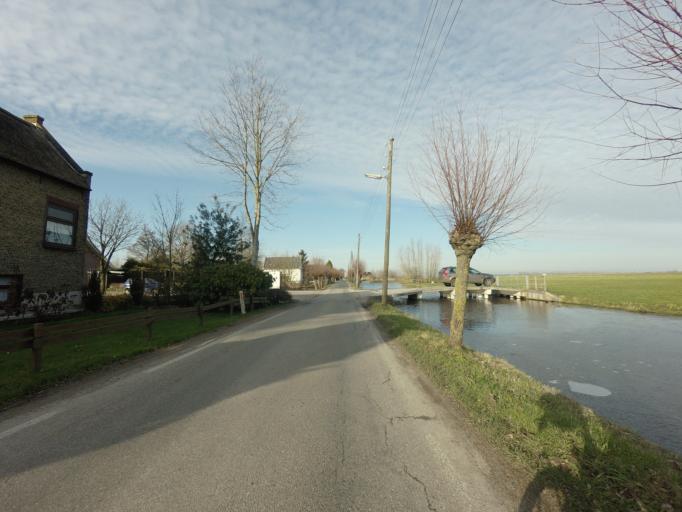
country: NL
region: South Holland
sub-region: Gemeente Vlist
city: Haastrecht
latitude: 52.0465
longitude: 4.7953
